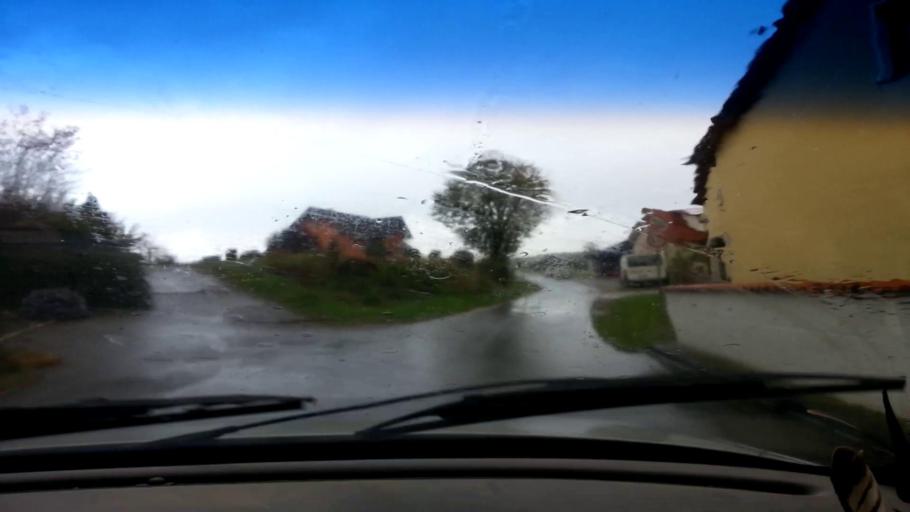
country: DE
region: Bavaria
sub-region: Upper Franconia
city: Priesendorf
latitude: 49.8646
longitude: 10.7233
